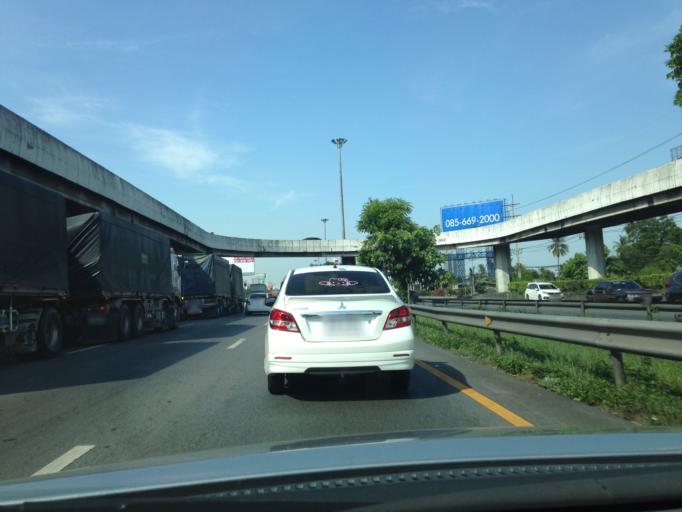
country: TH
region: Nonthaburi
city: Bang Yai
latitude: 13.8594
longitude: 100.4112
